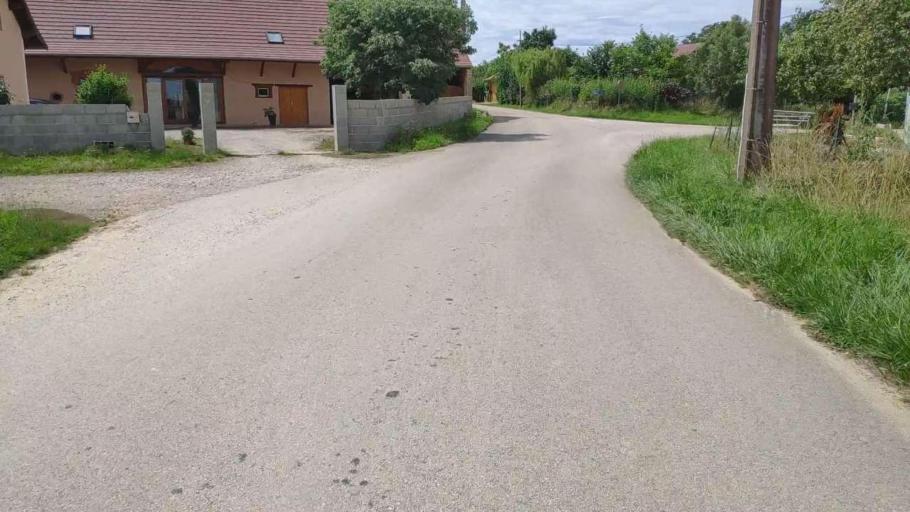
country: FR
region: Franche-Comte
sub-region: Departement du Jura
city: Chaussin
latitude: 46.8707
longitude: 5.4170
